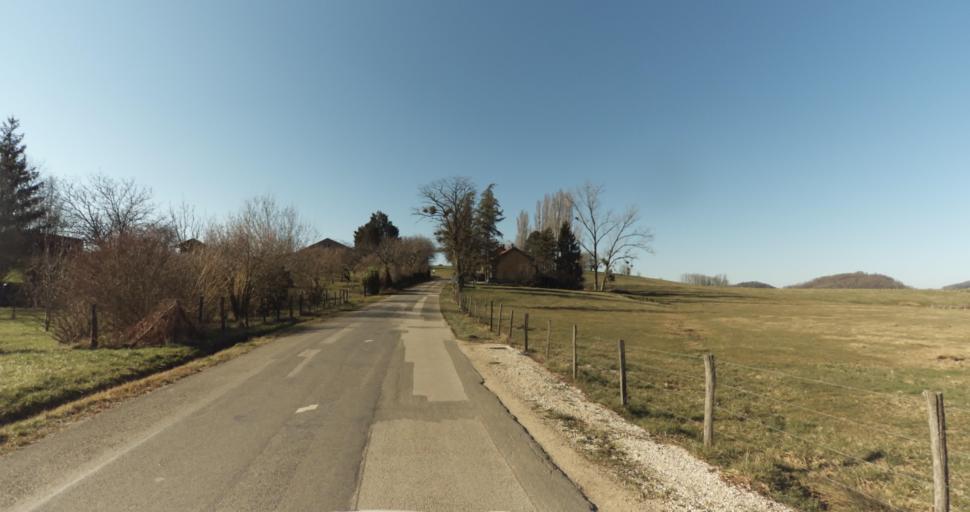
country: FR
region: Franche-Comte
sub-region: Departement du Jura
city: Montmorot
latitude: 46.6906
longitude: 5.5341
